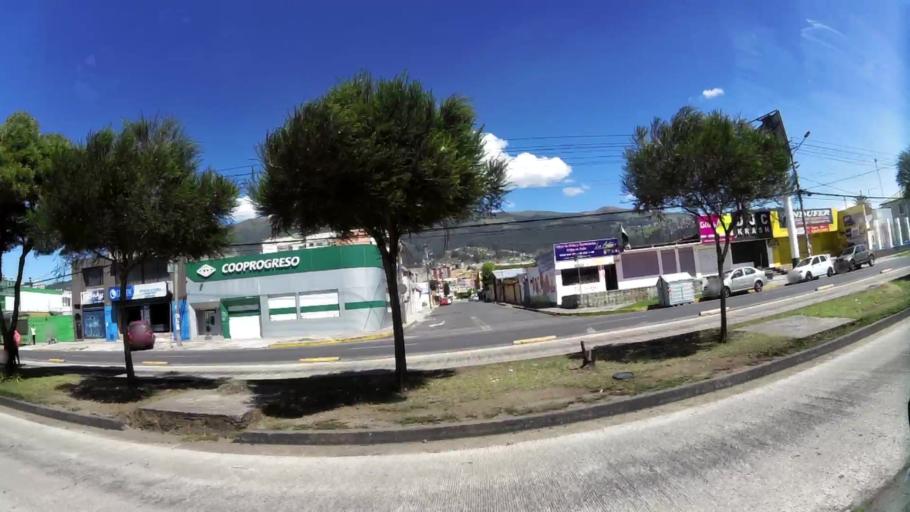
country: EC
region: Pichincha
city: Quito
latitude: -0.1382
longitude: -78.4932
